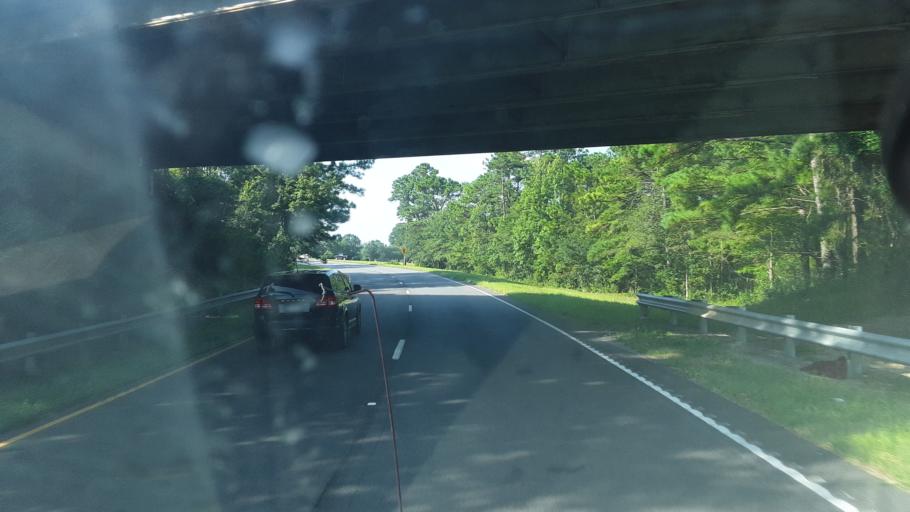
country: US
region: South Carolina
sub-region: Horry County
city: Little River
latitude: 33.8635
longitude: -78.6571
